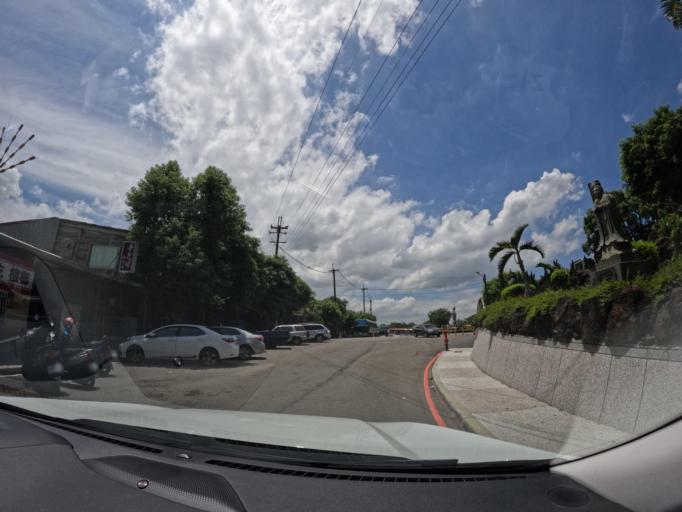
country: TW
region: Taiwan
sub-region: Taoyuan
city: Taoyuan
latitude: 25.0470
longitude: 121.3827
